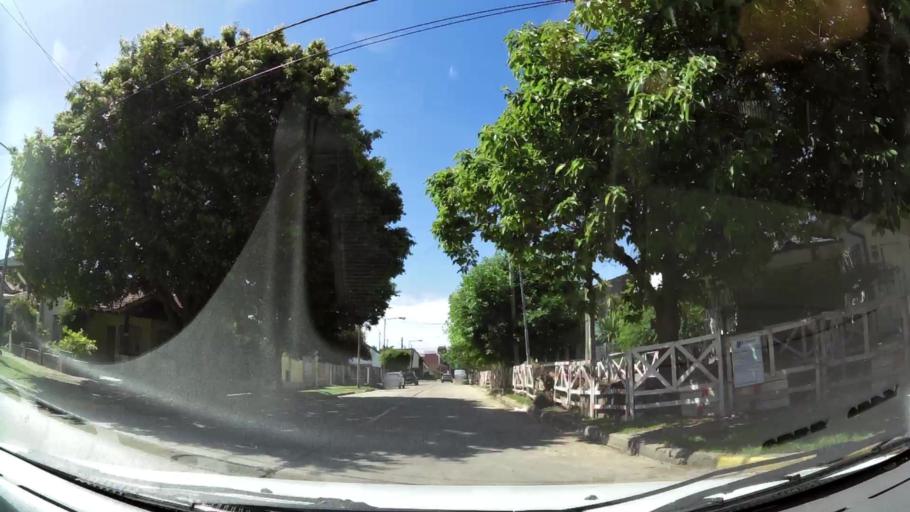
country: AR
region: Buenos Aires
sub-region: Partido de General San Martin
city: General San Martin
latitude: -34.5636
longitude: -58.5553
